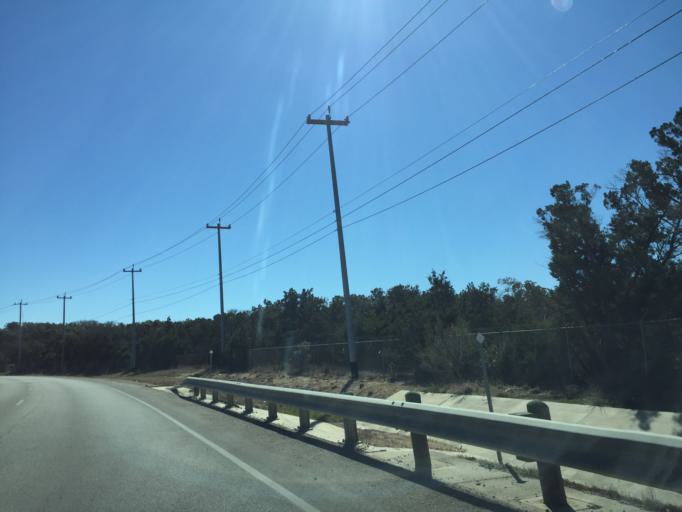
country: US
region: Texas
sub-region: Bexar County
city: Timberwood Park
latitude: 29.6900
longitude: -98.4481
